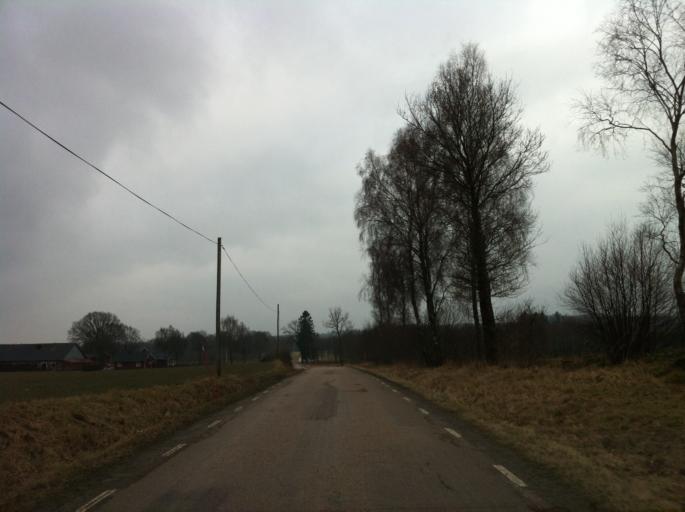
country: SE
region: Skane
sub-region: Svalovs Kommun
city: Kagerod
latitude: 56.0153
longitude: 13.1643
